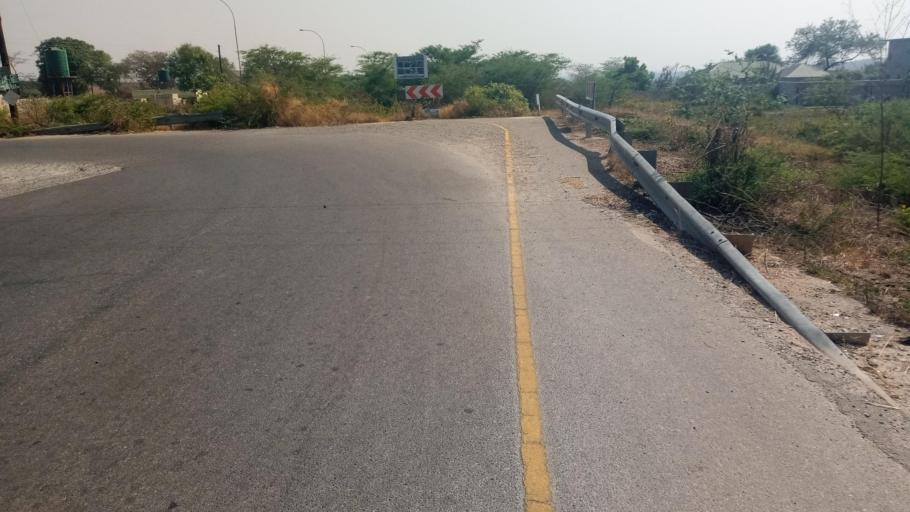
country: ZM
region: Lusaka
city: Lusaka
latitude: -15.4523
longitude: 28.4359
